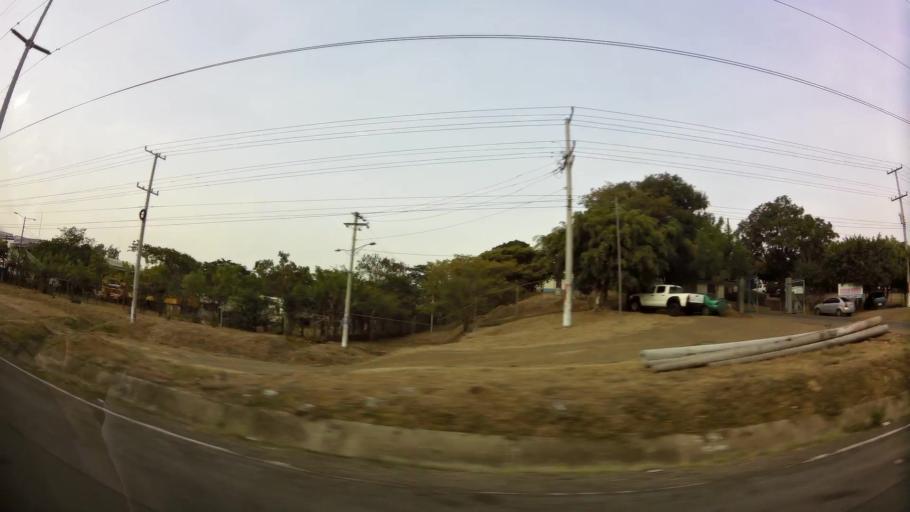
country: NI
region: Managua
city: Ciudad Sandino
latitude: 12.1637
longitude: -86.3403
